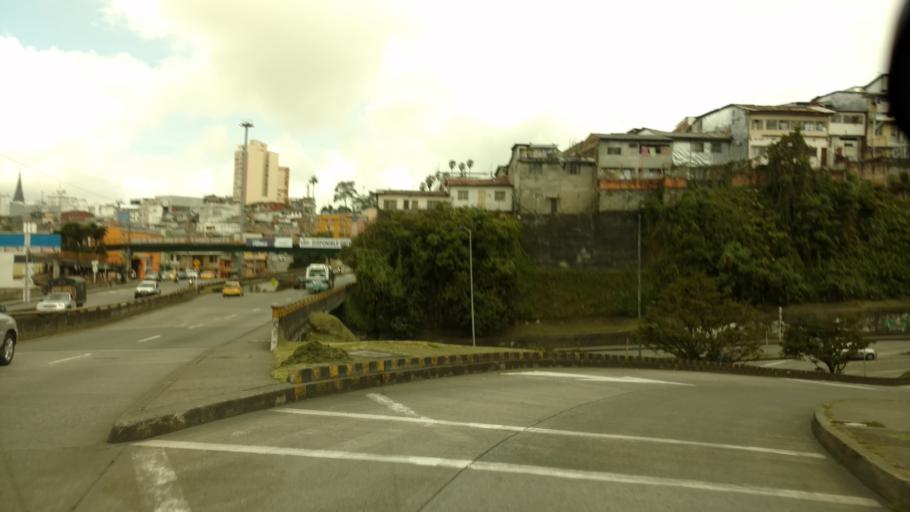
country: CO
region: Caldas
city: Manizales
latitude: 5.0656
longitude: -75.5074
